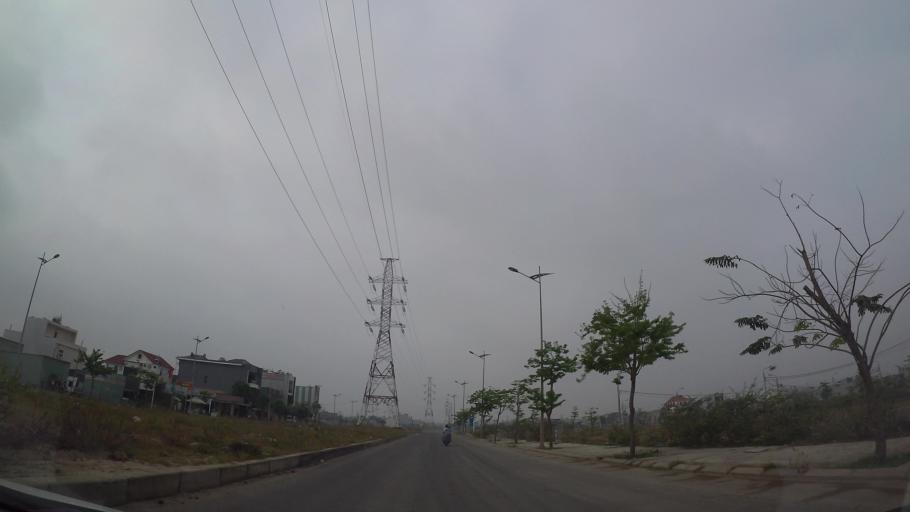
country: VN
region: Da Nang
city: Cam Le
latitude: 16.0144
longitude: 108.2265
